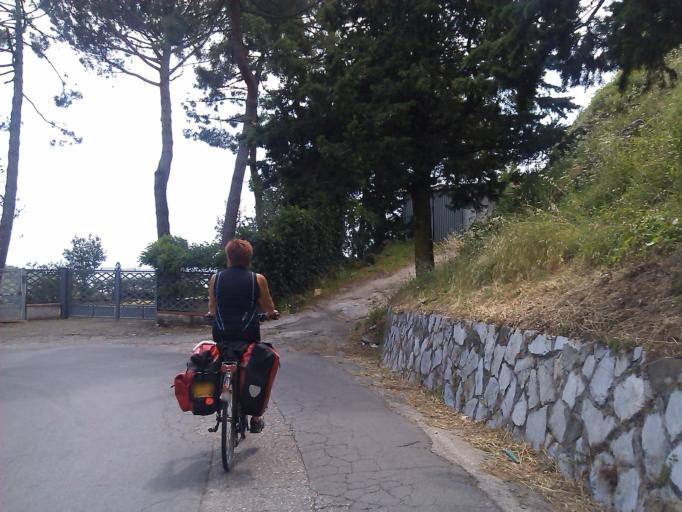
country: IT
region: Tuscany
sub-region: Provincia di Prato
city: Montemurlo
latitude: 43.9601
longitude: 11.0430
